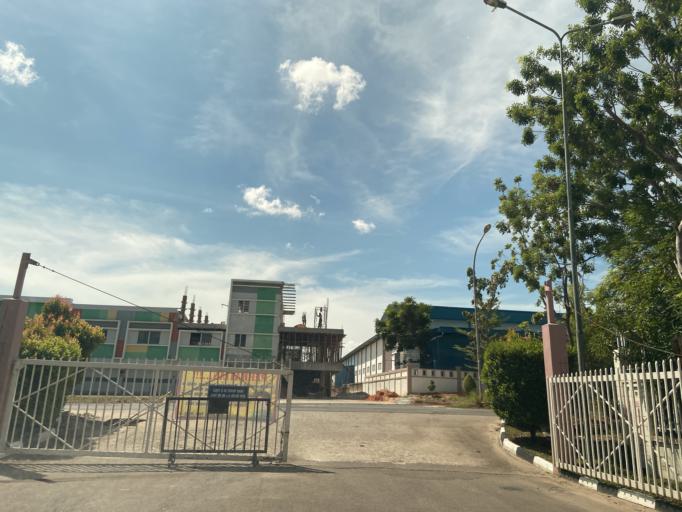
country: SG
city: Singapore
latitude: 1.1115
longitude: 104.0683
